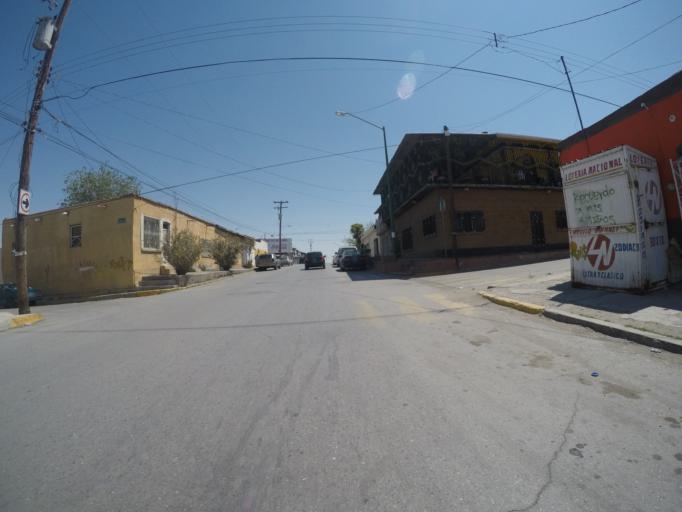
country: MX
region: Chihuahua
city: Ciudad Juarez
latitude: 31.7344
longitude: -106.4891
